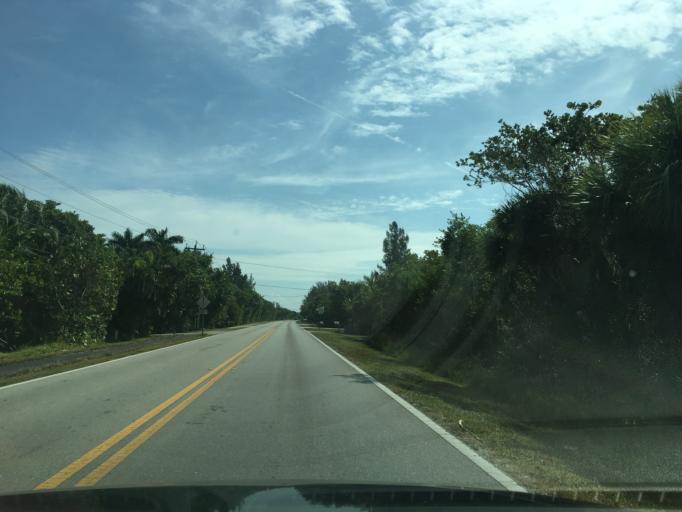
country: US
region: Florida
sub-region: Lee County
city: Saint James City
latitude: 26.4753
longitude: -82.1722
